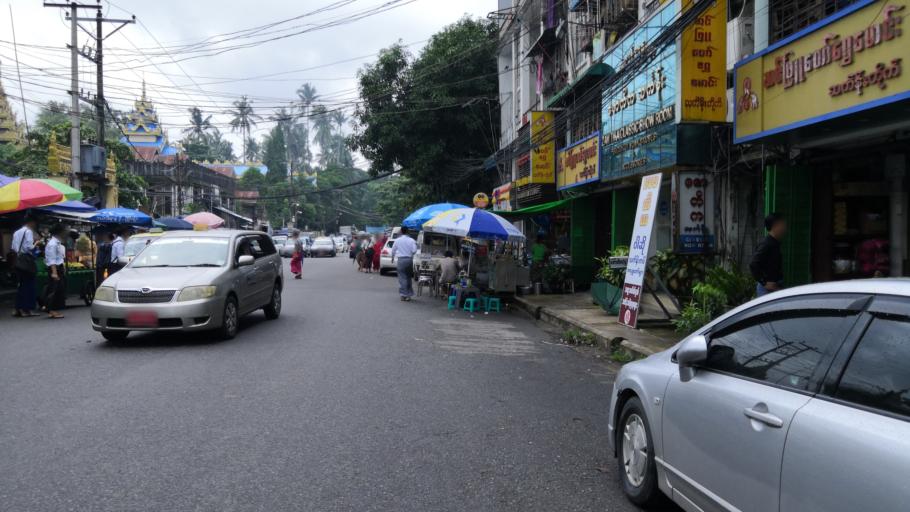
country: MM
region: Yangon
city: Yangon
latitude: 16.7986
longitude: 96.1542
